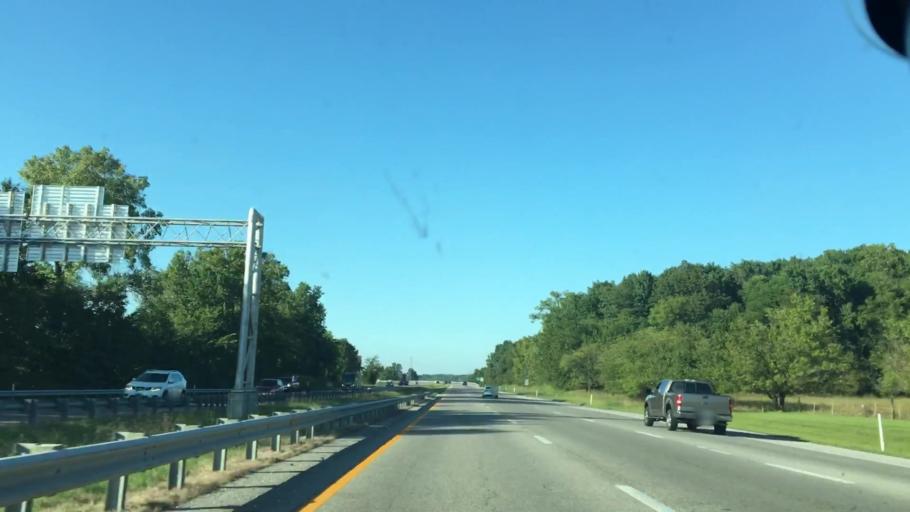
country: US
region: Kentucky
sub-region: Henderson County
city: Henderson
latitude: 37.8334
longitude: -87.5655
